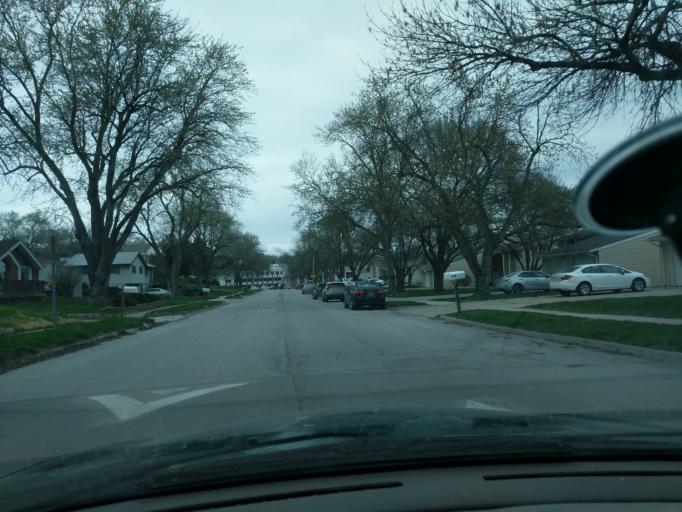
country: US
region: Nebraska
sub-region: Douglas County
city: Ralston
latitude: 41.2320
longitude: -96.0943
